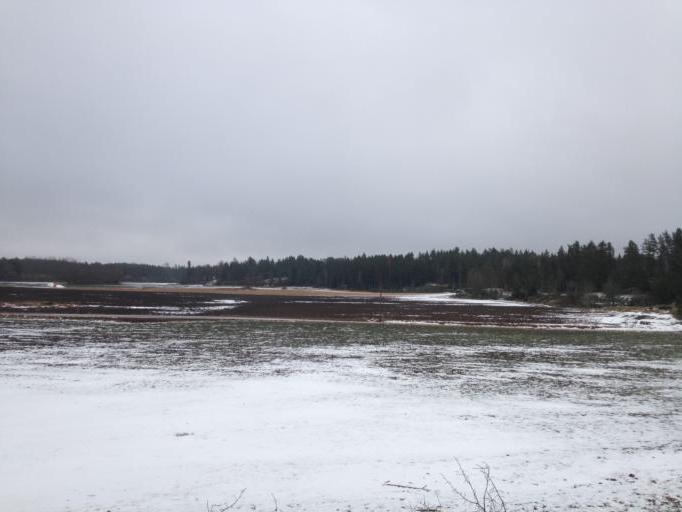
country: SE
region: OEstergoetland
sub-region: Norrkopings Kommun
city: Krokek
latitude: 58.5542
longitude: 16.5541
